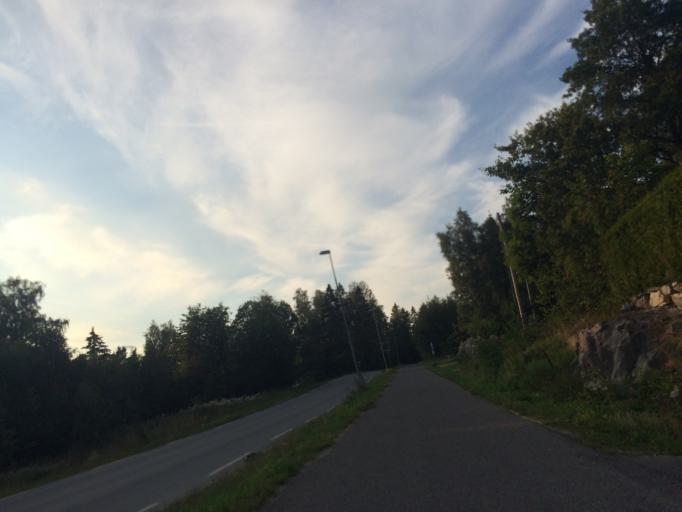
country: NO
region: Akershus
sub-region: Ski
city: Ski
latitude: 59.7012
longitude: 10.8452
